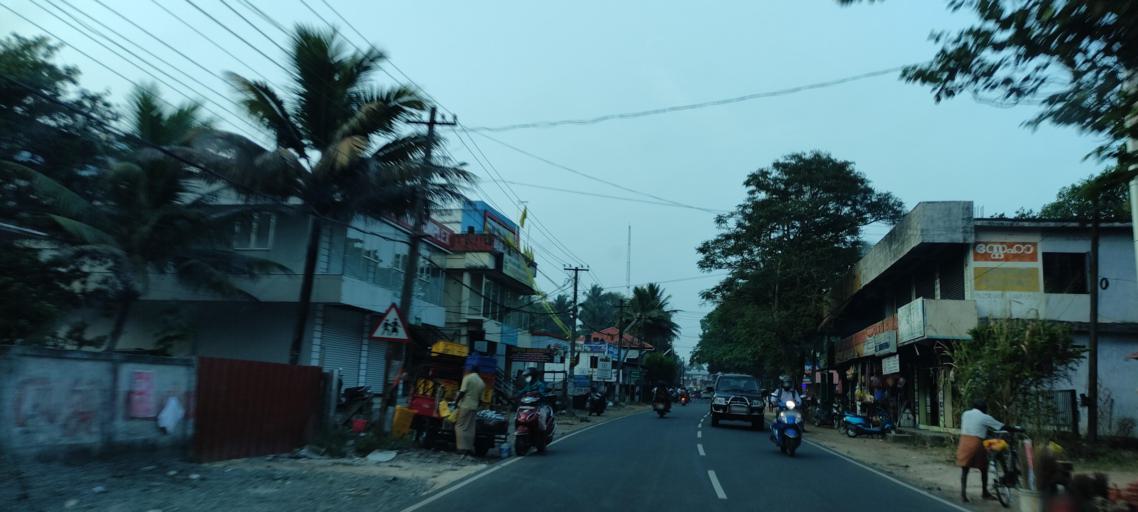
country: IN
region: Kerala
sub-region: Alappuzha
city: Mavelikara
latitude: 9.3088
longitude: 76.5341
